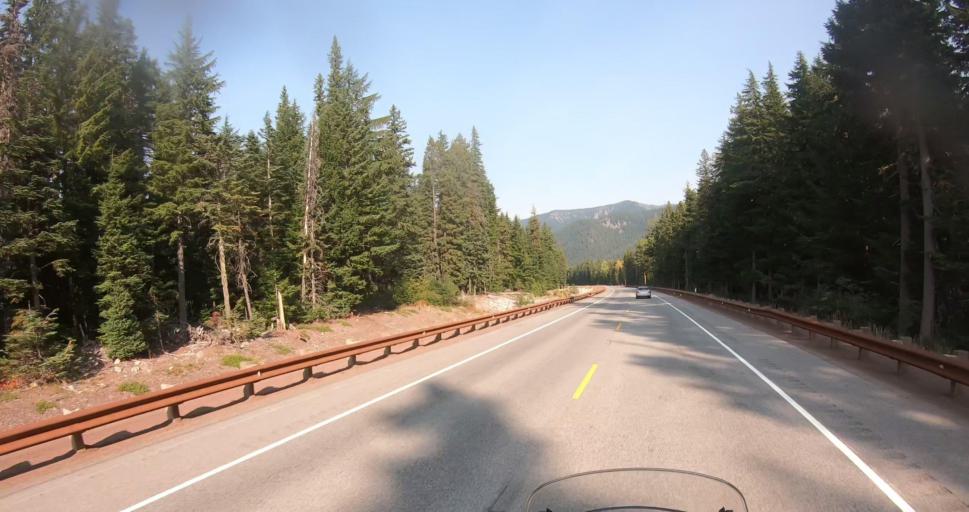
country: US
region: Oregon
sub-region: Hood River County
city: Odell
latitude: 45.3219
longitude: -121.6007
